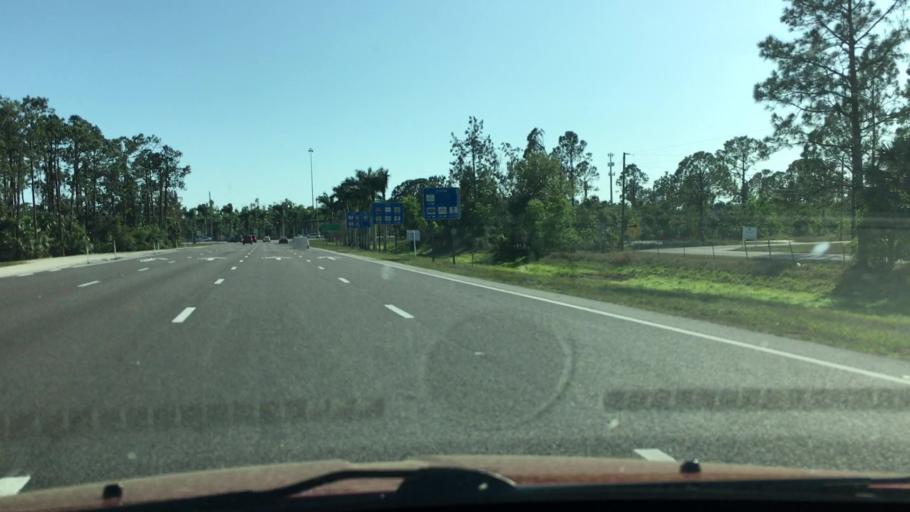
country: US
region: Florida
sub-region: Collier County
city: Vineyards
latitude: 26.2141
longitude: -81.7370
